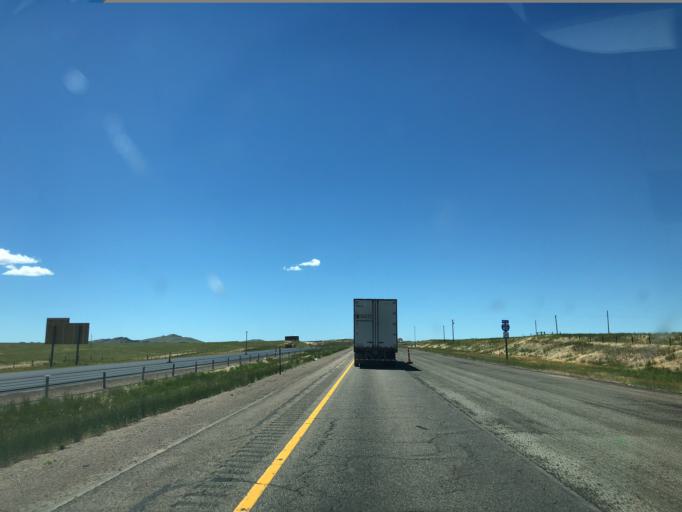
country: US
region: Wyoming
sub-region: Laramie County
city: Cheyenne
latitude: 41.0989
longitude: -105.1274
